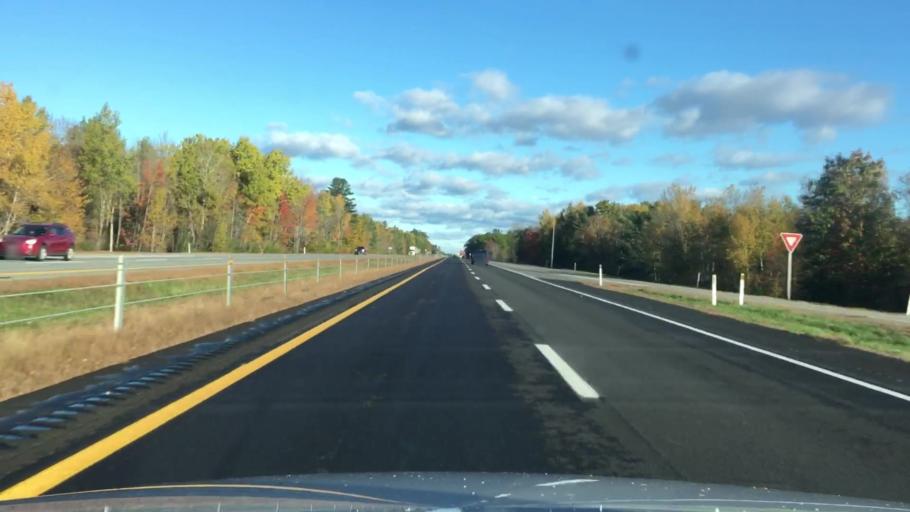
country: US
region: Maine
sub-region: Penobscot County
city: Orono
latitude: 44.9048
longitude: -68.6928
